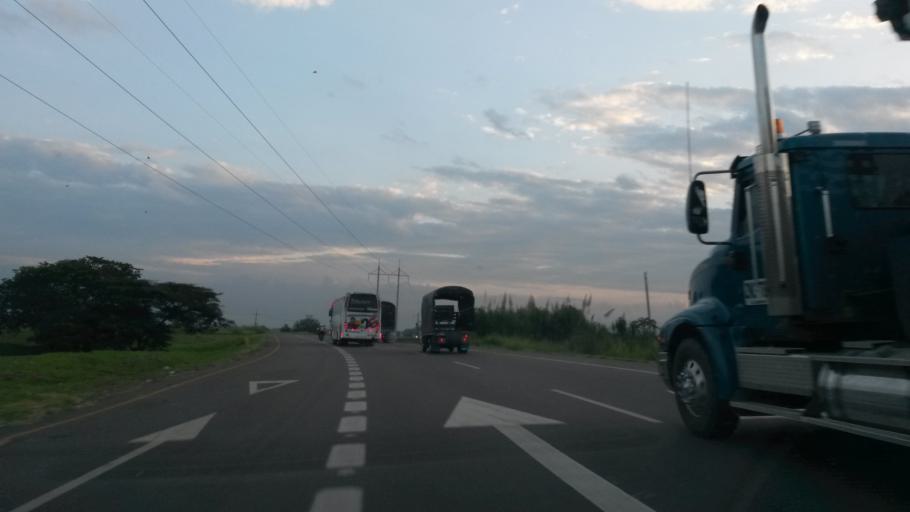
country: CO
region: Cauca
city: Caloto
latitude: 3.0956
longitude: -76.4695
